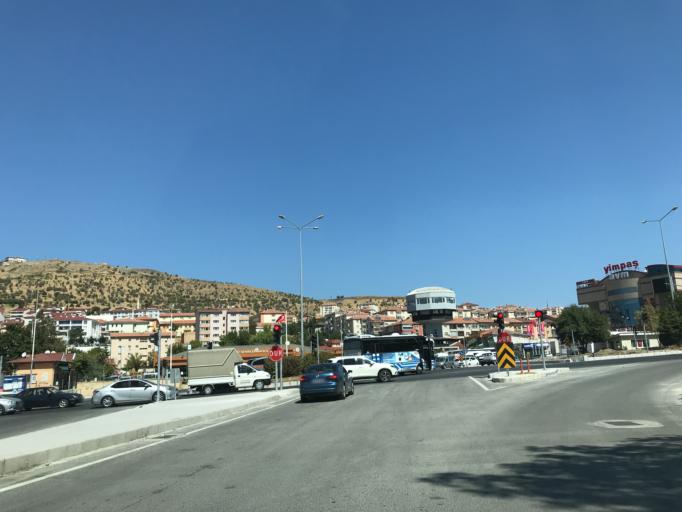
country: TR
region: Yozgat
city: Yozgat
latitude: 39.8224
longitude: 34.8173
